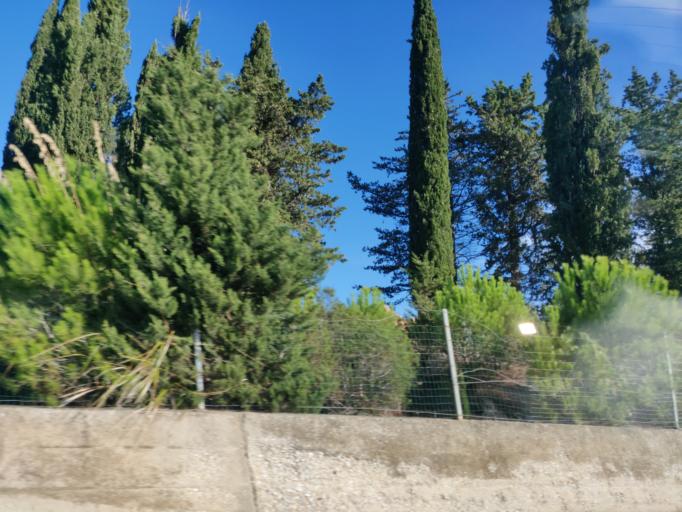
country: IT
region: Tuscany
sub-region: Provincia di Grosseto
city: Scarlino Scalo
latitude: 42.9629
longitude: 10.8418
